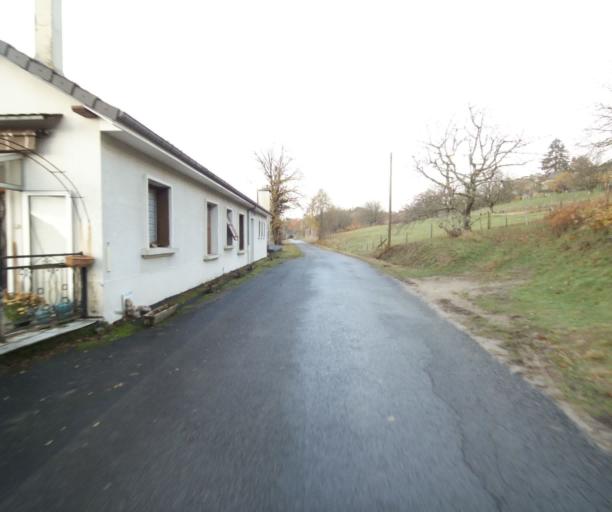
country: FR
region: Limousin
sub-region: Departement de la Correze
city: Cornil
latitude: 45.2190
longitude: 1.6616
